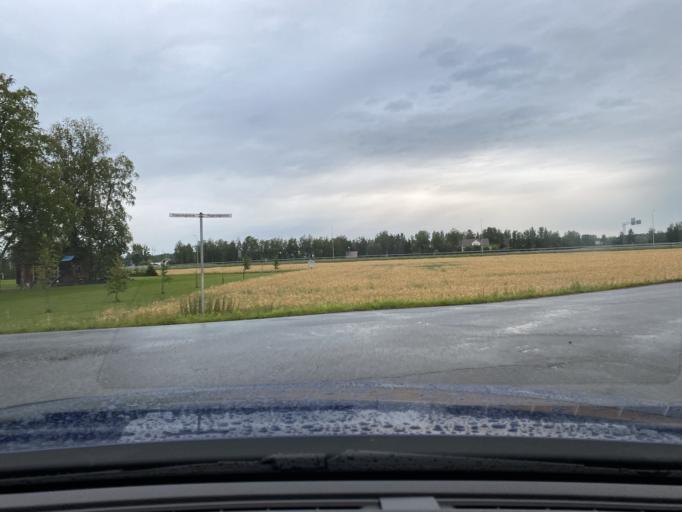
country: FI
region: Ostrobothnia
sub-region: Kyroenmaa
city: Laihia
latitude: 62.9835
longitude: 21.9939
